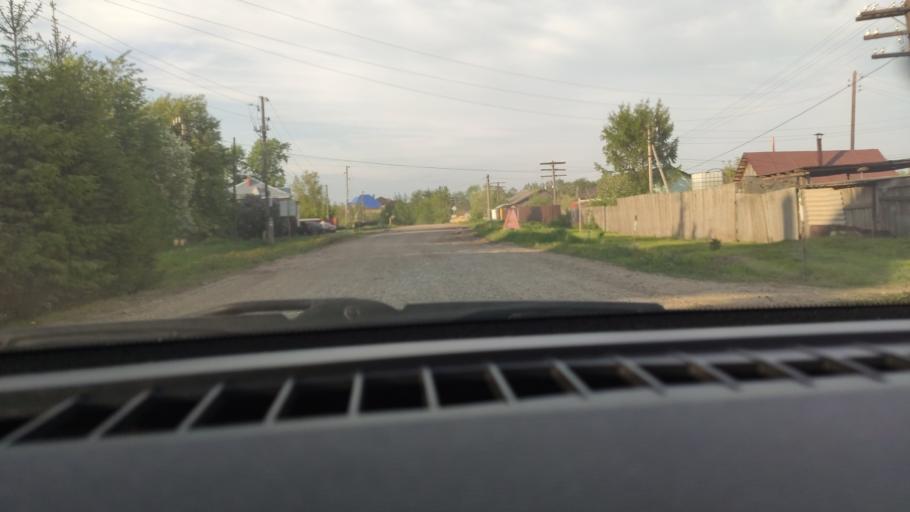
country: RU
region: Perm
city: Kultayevo
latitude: 57.9290
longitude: 56.0142
